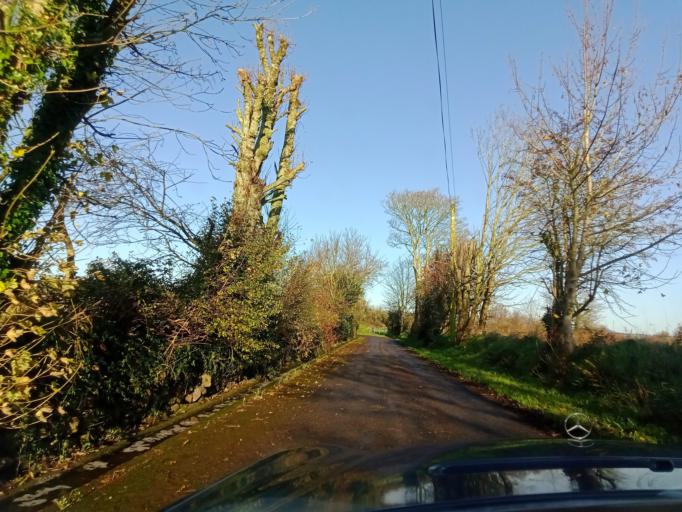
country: IE
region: Leinster
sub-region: Kilkenny
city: Mooncoin
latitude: 52.2927
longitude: -7.2061
